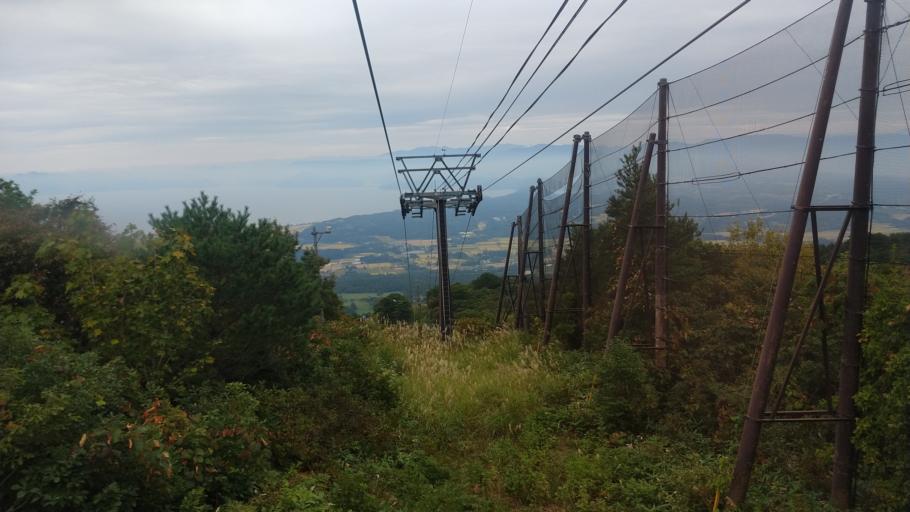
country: JP
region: Fukushima
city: Inawashiro
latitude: 37.5898
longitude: 140.0623
